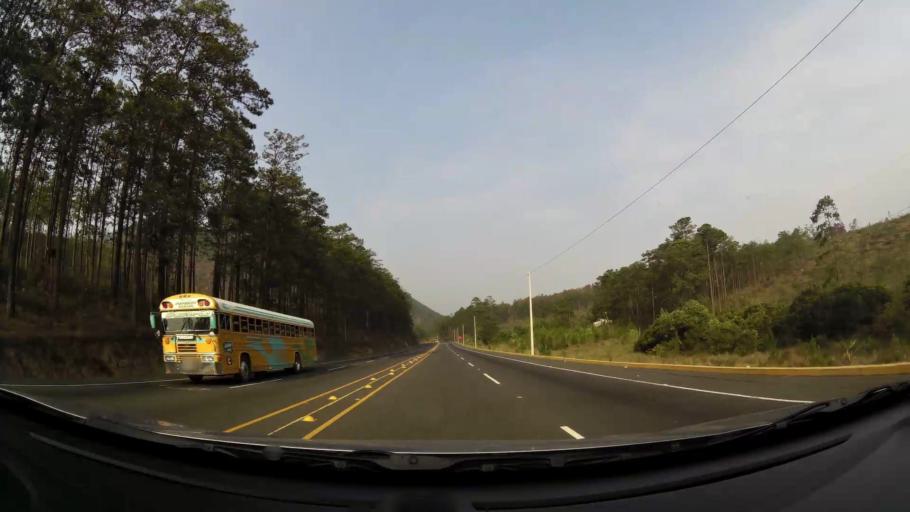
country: HN
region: Francisco Morazan
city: Zambrano
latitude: 14.2892
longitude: -87.4431
